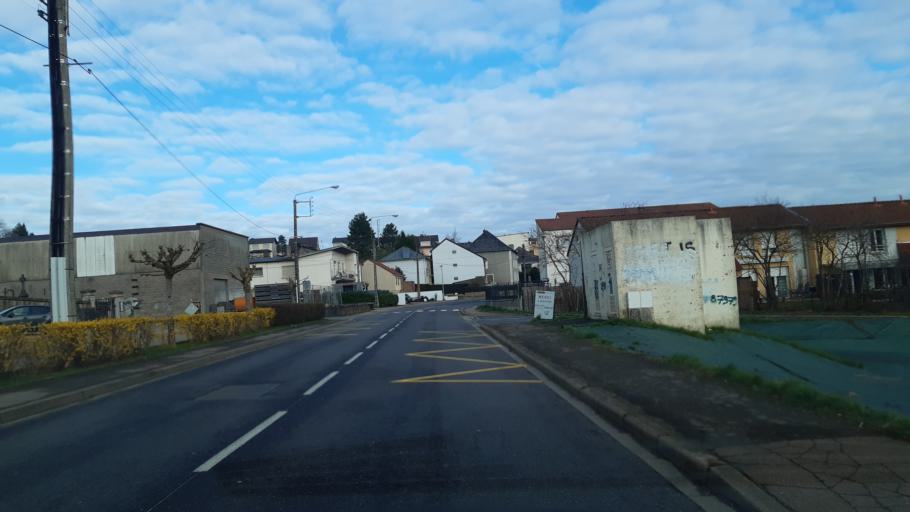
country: FR
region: Lorraine
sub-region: Departement de la Moselle
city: Audun-le-Tiche
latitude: 49.4724
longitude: 5.9505
